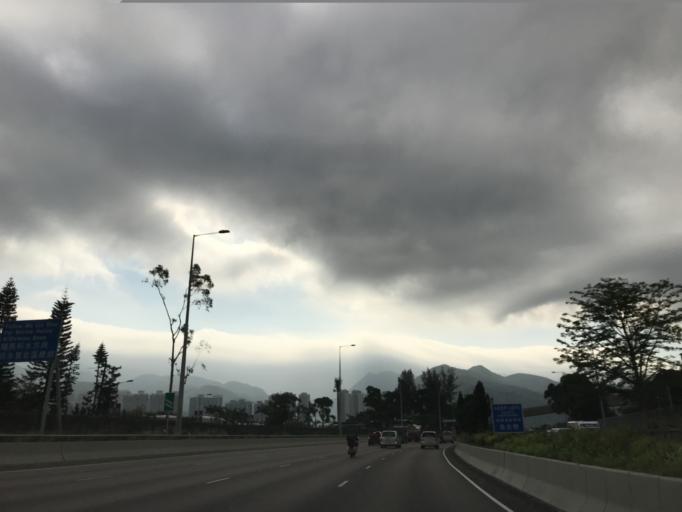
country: HK
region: Sha Tin
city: Sha Tin
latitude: 22.4225
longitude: 114.2127
